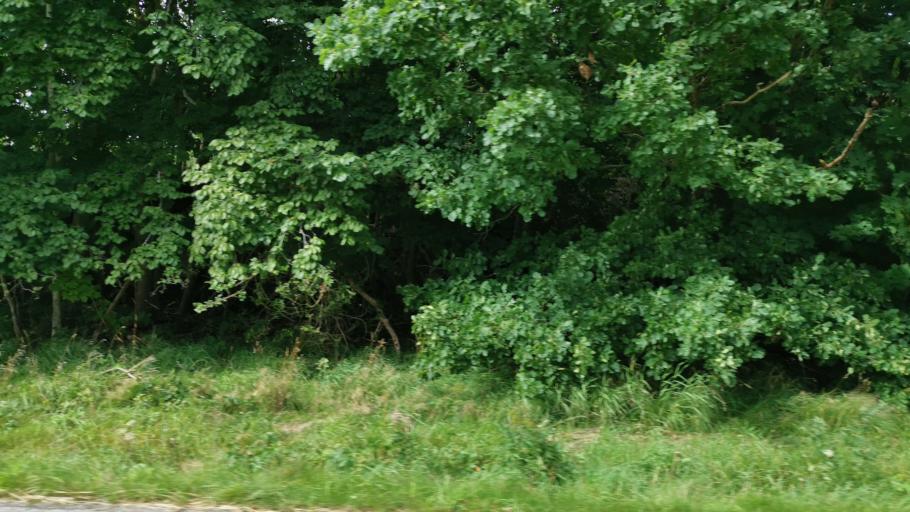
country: SE
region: Vaestra Goetaland
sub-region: Lysekils Kommun
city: Brastad
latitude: 58.4681
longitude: 11.4605
